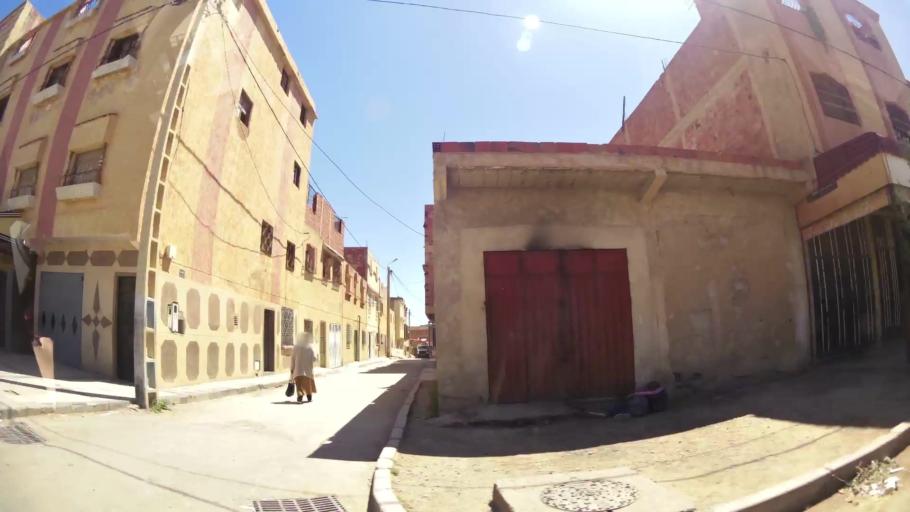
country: MA
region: Oriental
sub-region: Oujda-Angad
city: Oujda
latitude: 34.6626
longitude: -1.8812
